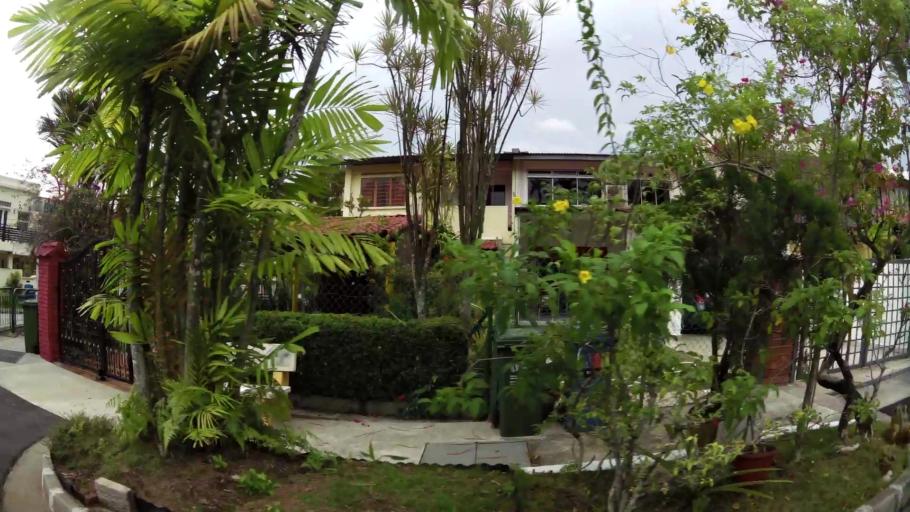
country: SG
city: Singapore
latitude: 1.3801
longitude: 103.8300
